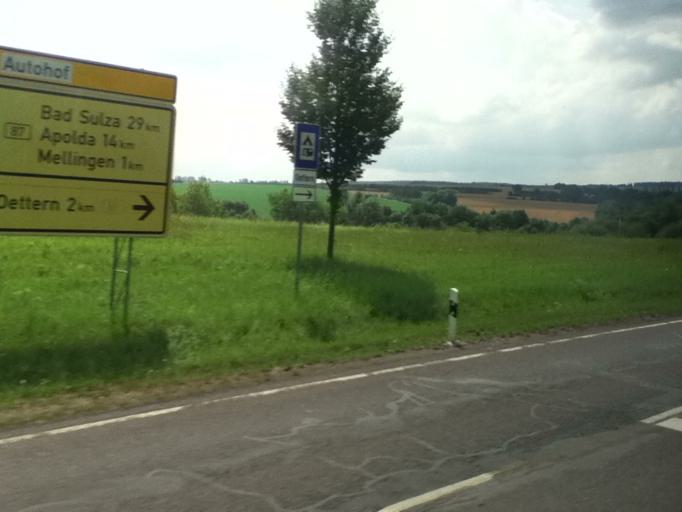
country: DE
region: Thuringia
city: Mellingen
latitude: 50.9309
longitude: 11.3883
